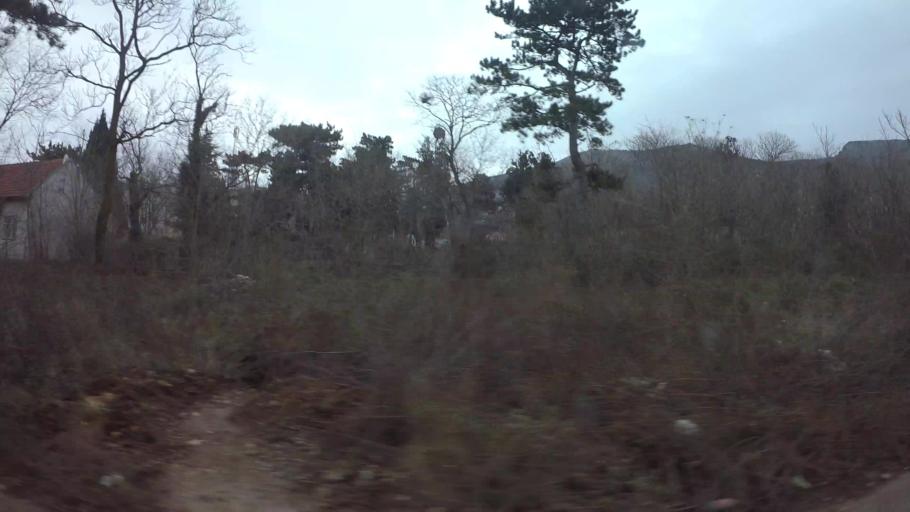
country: BA
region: Federation of Bosnia and Herzegovina
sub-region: Hercegovacko-Bosanski Kanton
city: Mostar
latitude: 43.3512
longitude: 17.8111
